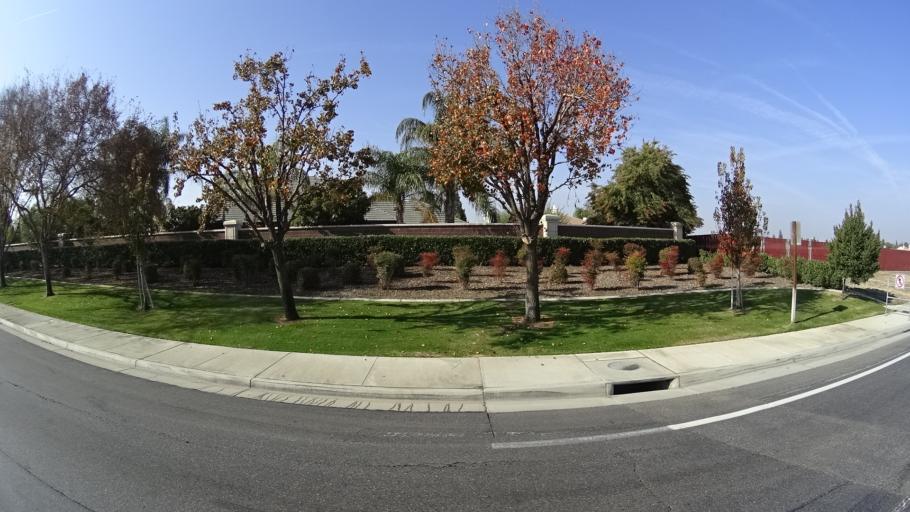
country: US
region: California
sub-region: Kern County
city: Greenacres
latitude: 35.3600
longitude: -119.1161
